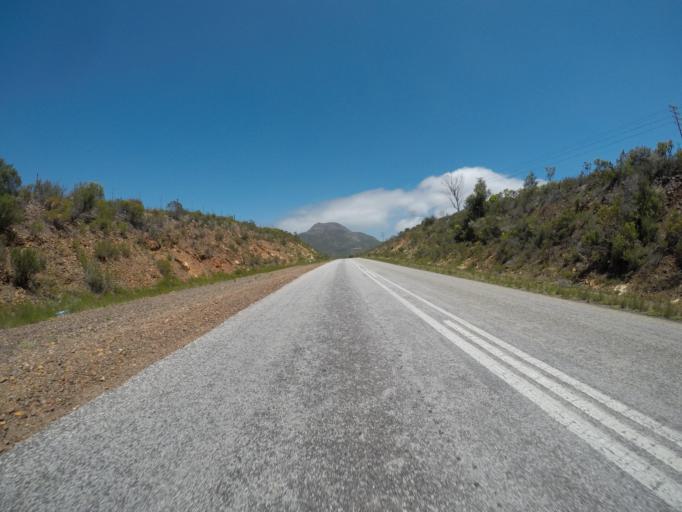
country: ZA
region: Eastern Cape
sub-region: Cacadu District Municipality
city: Kareedouw
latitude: -33.9392
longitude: 24.2660
